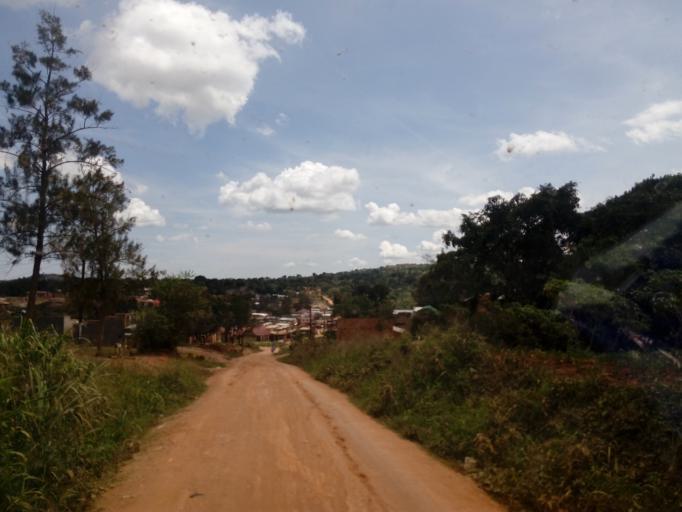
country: UG
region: Central Region
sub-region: Mubende District
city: Mubende
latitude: 0.4495
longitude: 31.6901
